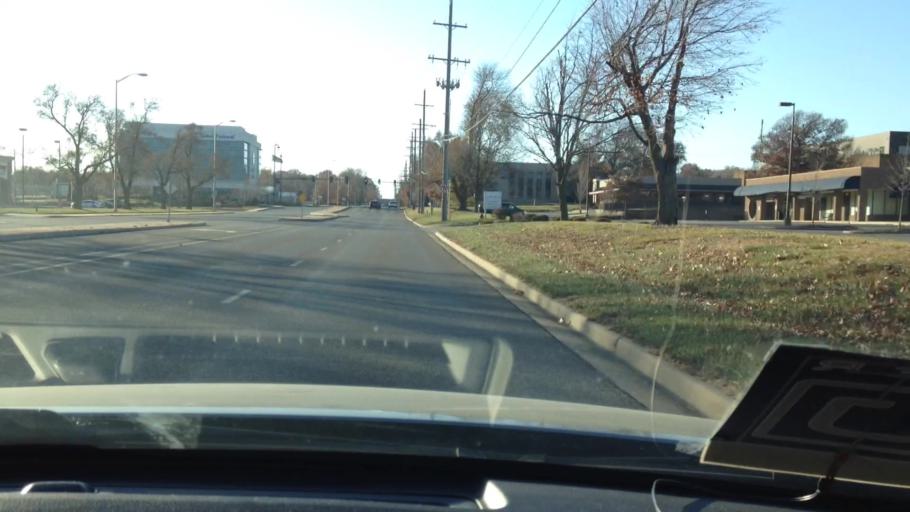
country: US
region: Kansas
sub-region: Johnson County
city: Leawood
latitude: 38.9568
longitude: -94.6463
